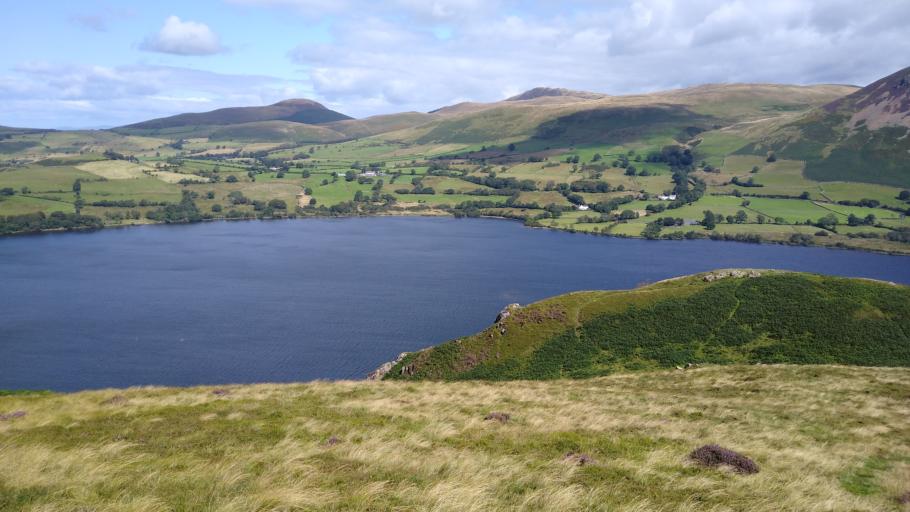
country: GB
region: England
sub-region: Cumbria
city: Frizington
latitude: 54.5210
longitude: -3.3944
